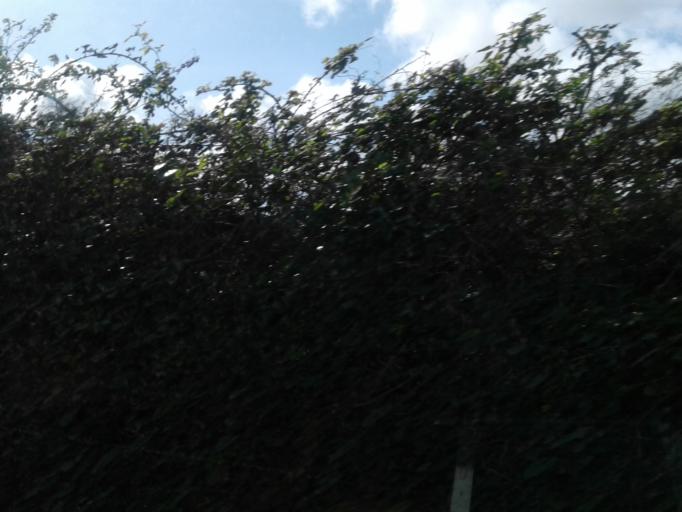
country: IE
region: Leinster
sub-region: Fingal County
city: Swords
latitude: 53.4811
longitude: -6.2830
